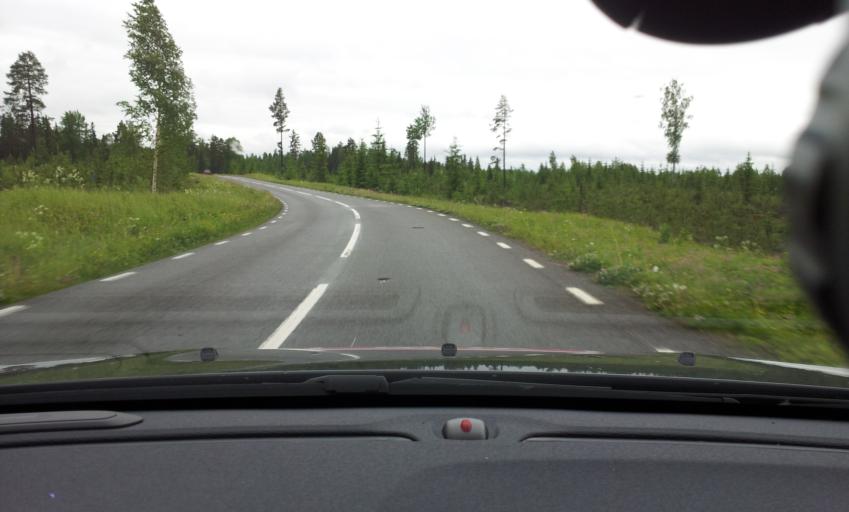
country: SE
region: Jaemtland
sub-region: Stroemsunds Kommun
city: Stroemsund
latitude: 63.4998
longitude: 15.4600
